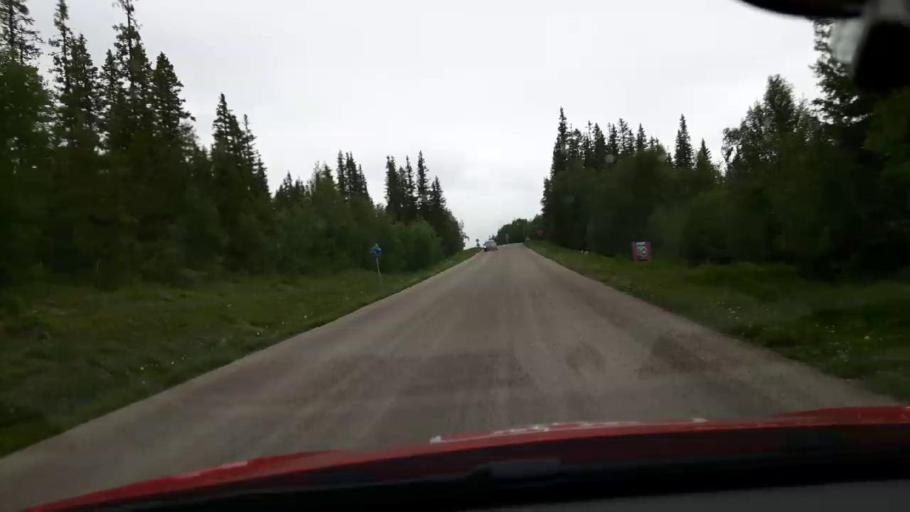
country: NO
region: Nord-Trondelag
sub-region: Meraker
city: Meraker
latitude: 63.2864
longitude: 12.3464
